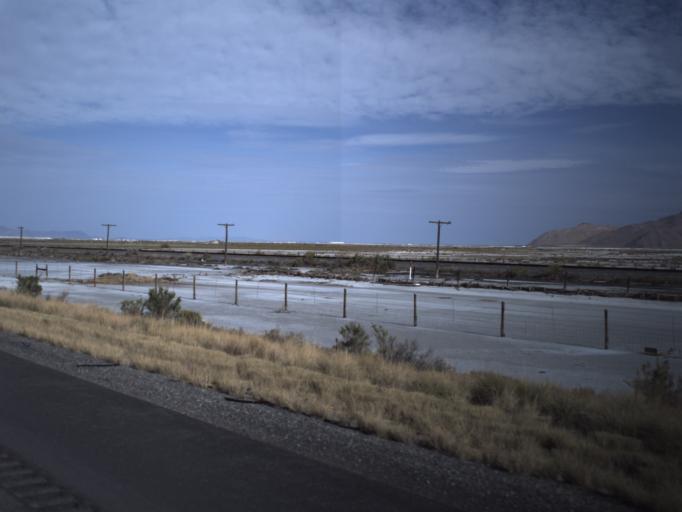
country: US
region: Utah
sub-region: Tooele County
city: Grantsville
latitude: 40.7003
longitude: -112.4863
